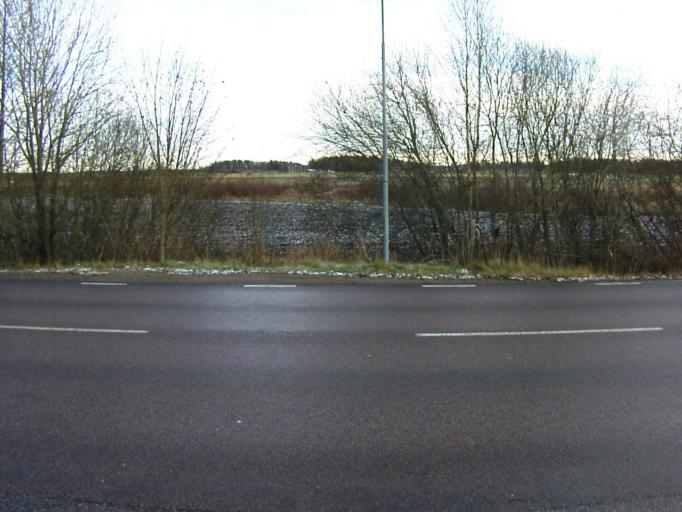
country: SE
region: Soedermanland
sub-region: Eskilstuna Kommun
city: Hallbybrunn
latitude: 59.3830
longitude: 16.4350
